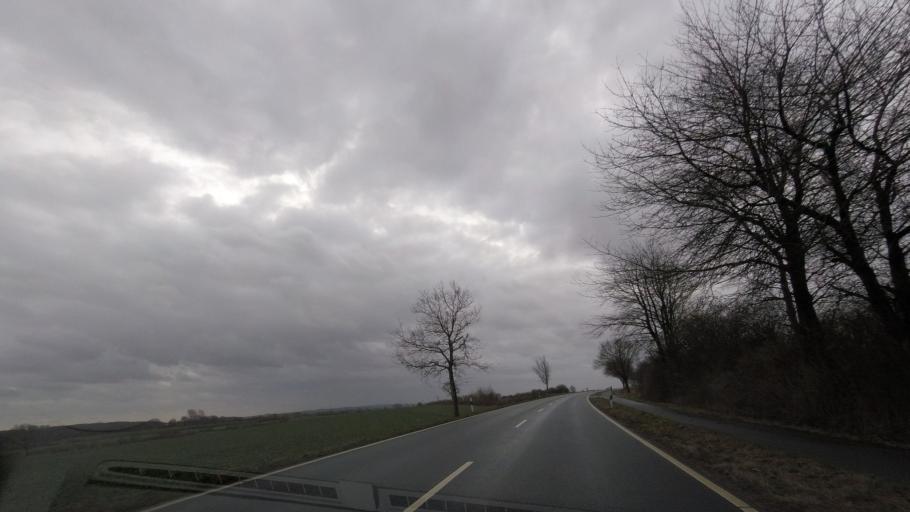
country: DE
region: Schleswig-Holstein
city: Tolk
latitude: 54.5690
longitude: 9.6449
